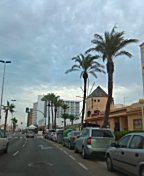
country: ES
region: Murcia
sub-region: Murcia
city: La Manga del Mar Menor
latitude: 37.6987
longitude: -0.7405
